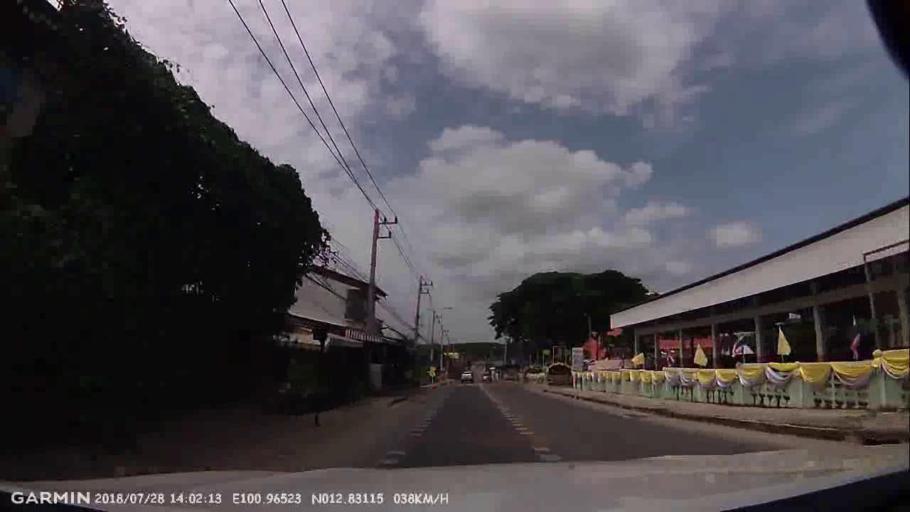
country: TH
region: Chon Buri
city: Phatthaya
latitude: 12.8312
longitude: 100.9653
